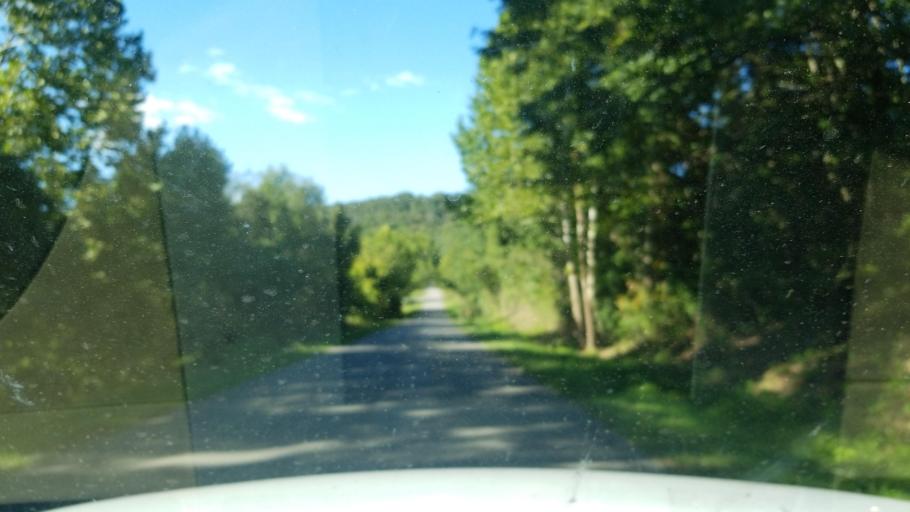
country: US
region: Illinois
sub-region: Hardin County
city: Elizabethtown
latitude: 37.5931
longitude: -88.3650
